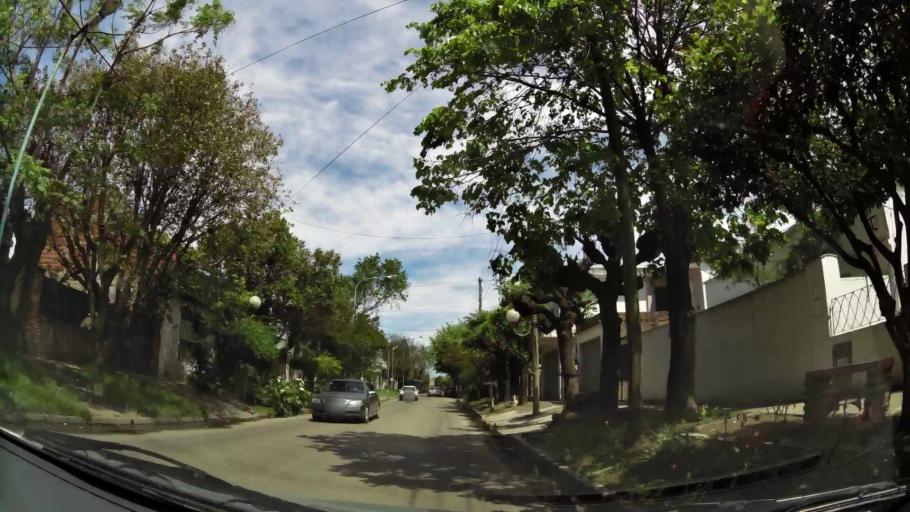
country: AR
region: Buenos Aires
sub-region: Partido de Quilmes
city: Quilmes
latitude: -34.7541
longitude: -58.2960
